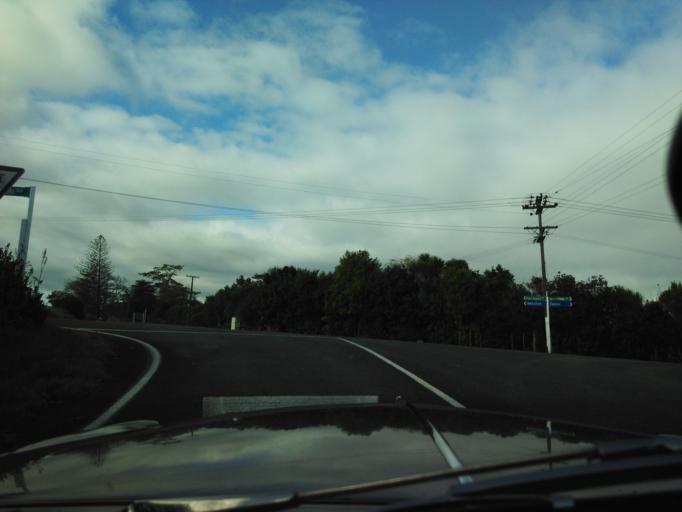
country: NZ
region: Auckland
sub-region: Auckland
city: Wellsford
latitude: -36.2827
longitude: 174.4342
